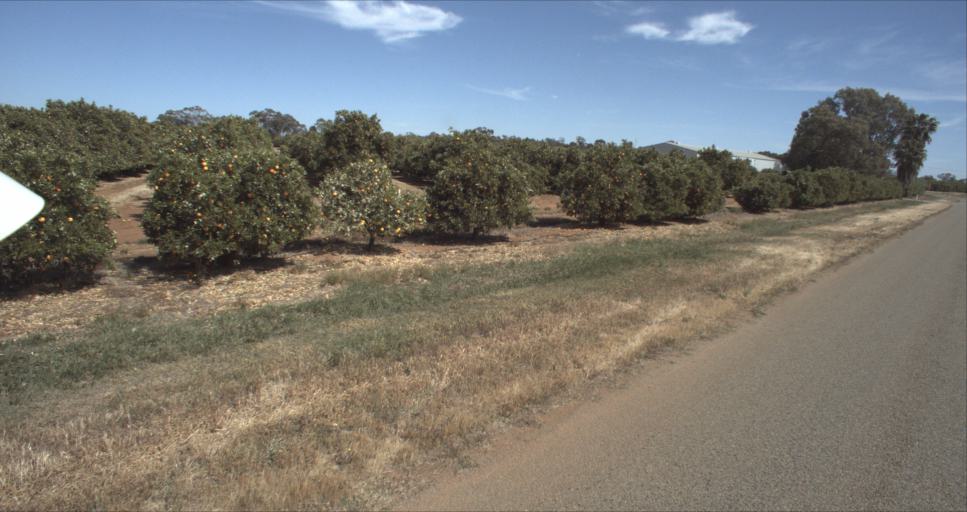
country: AU
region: New South Wales
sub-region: Leeton
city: Leeton
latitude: -34.5897
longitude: 146.4623
